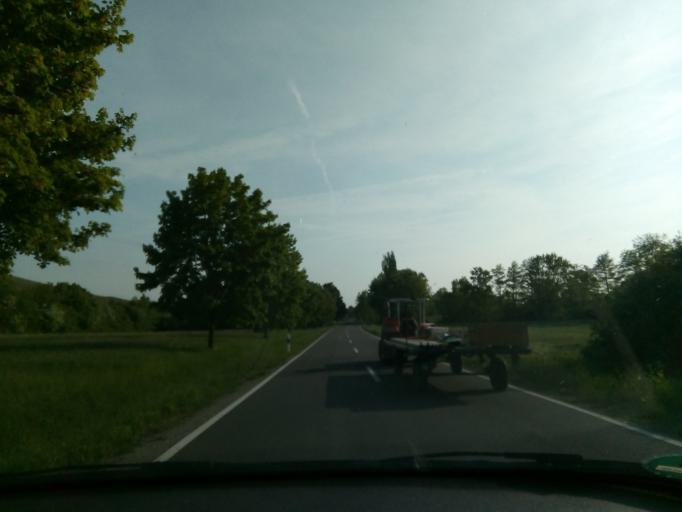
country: DE
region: Bavaria
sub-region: Regierungsbezirk Unterfranken
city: Oberschwarzach
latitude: 49.8644
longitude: 10.4197
